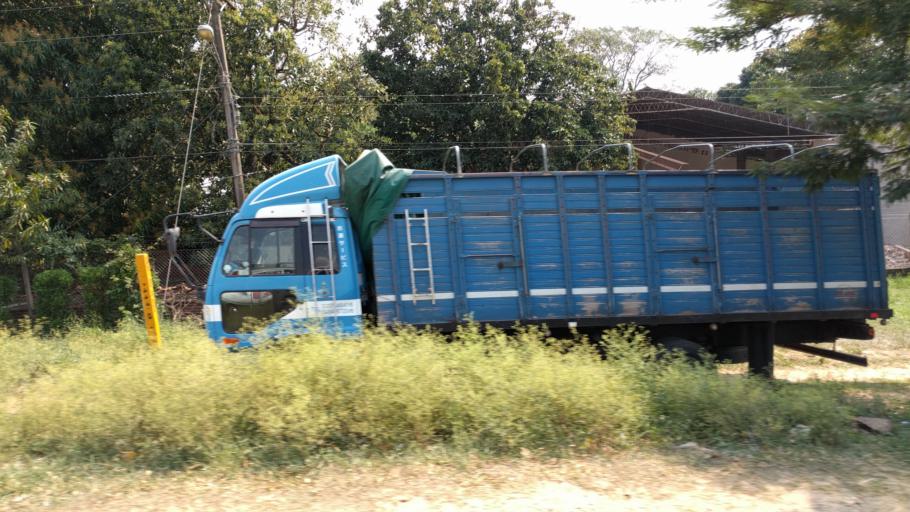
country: BO
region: Santa Cruz
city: Santa Rita
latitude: -17.9693
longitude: -63.3636
